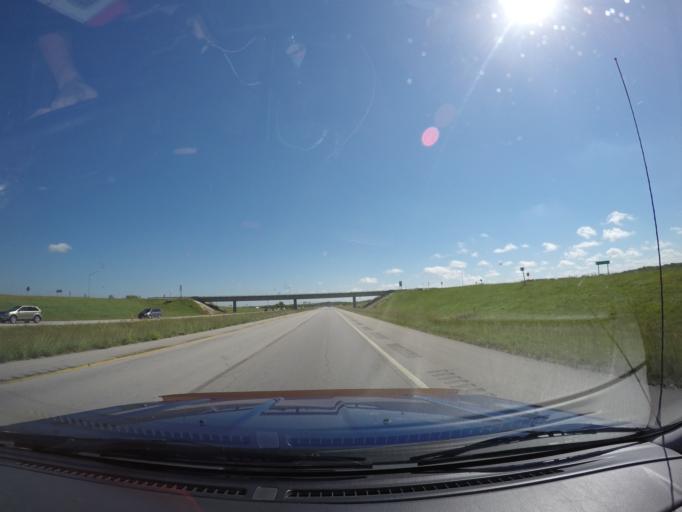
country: US
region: Kansas
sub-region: Douglas County
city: Eudora
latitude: 38.9348
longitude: -95.1509
